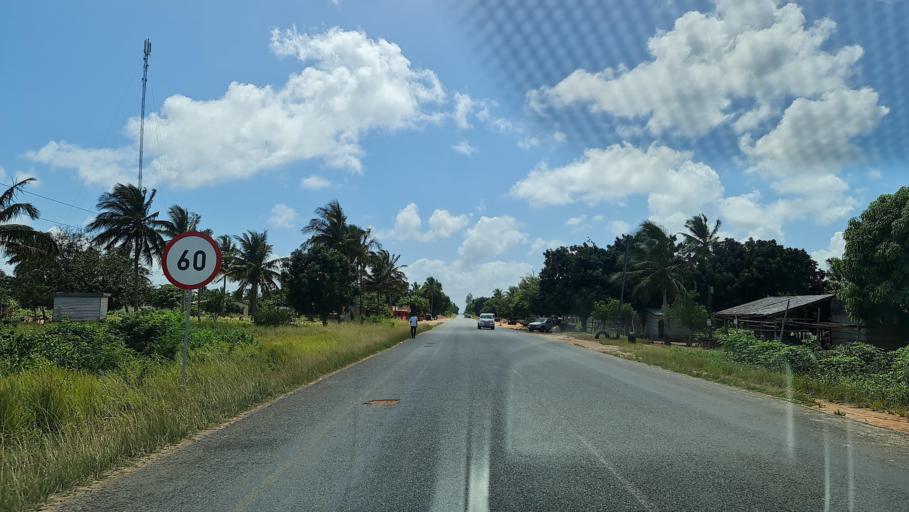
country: MZ
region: Inhambane
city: Maxixe
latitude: -24.5300
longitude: 34.9507
